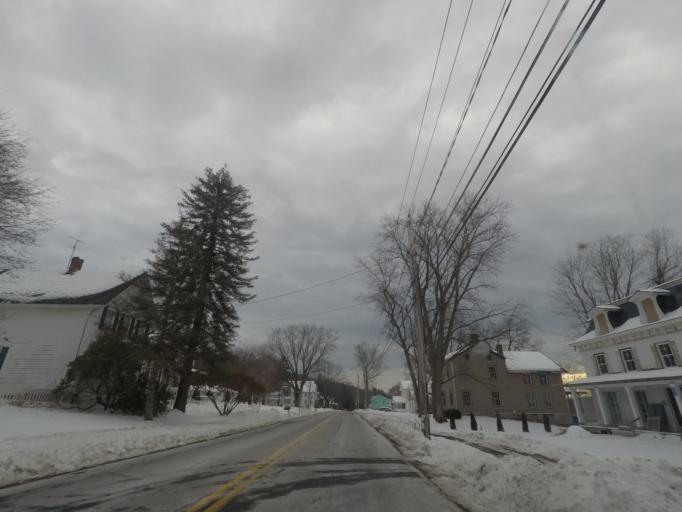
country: US
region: New York
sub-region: Rensselaer County
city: Castleton-on-Hudson
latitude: 42.4791
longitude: -73.7701
